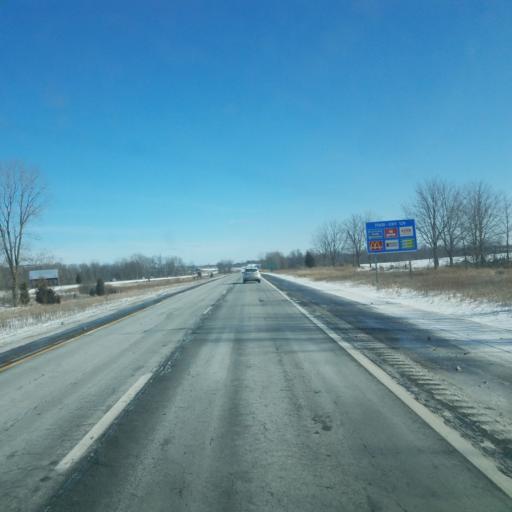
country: US
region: Michigan
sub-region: Livingston County
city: Fowlerville
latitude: 42.6460
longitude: -84.0907
